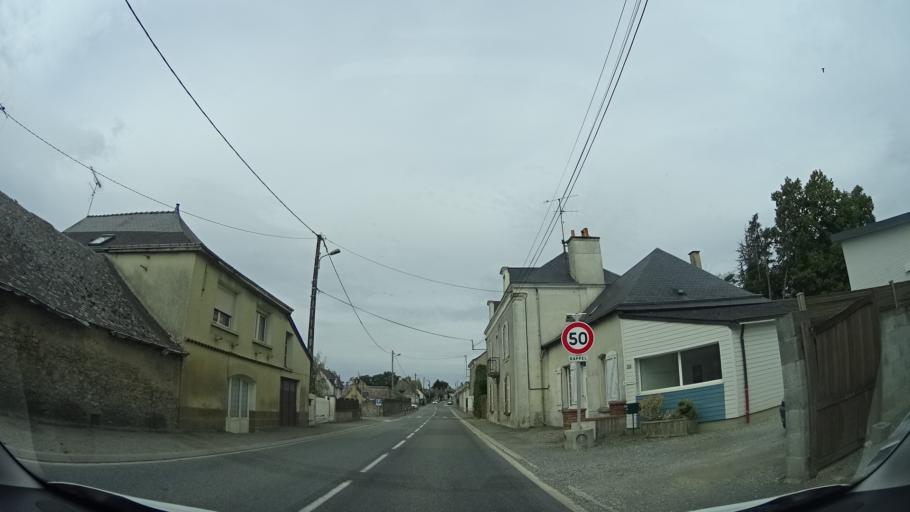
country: FR
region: Pays de la Loire
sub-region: Departement de la Sarthe
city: Auvers-le-Hamon
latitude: 47.8905
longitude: -0.4177
